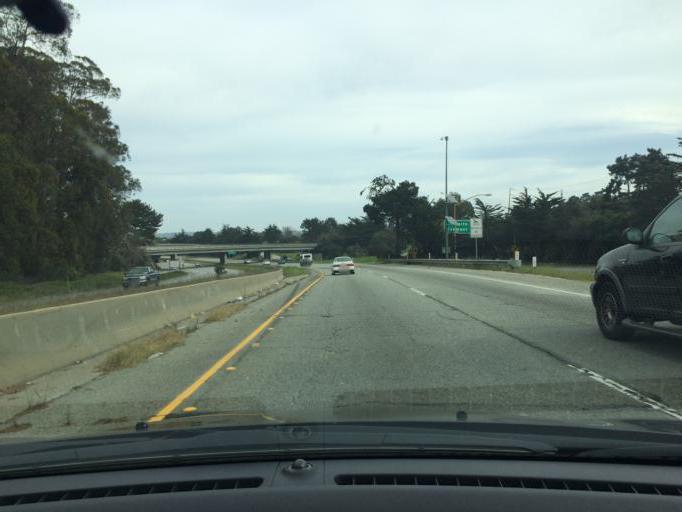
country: US
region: California
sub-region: Monterey County
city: Monterey
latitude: 36.5942
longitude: -121.8712
